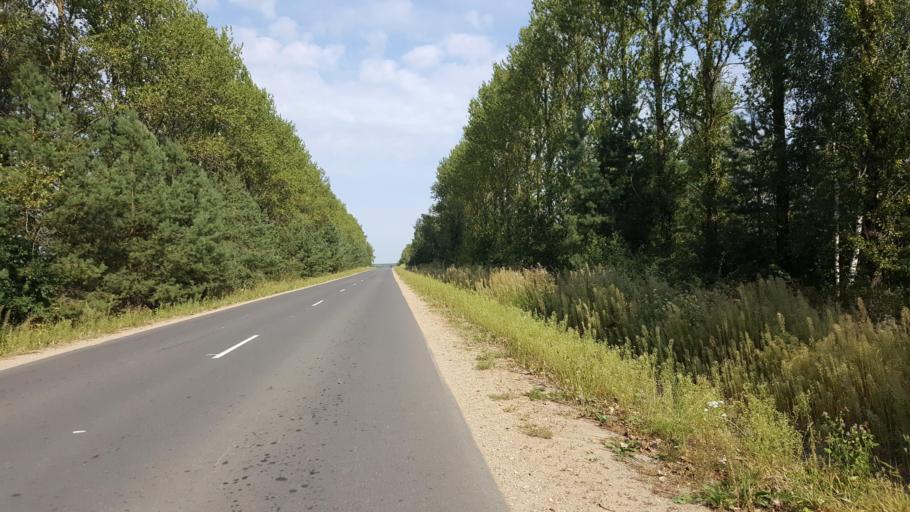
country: BY
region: Brest
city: Kamyanyets
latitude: 52.4535
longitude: 23.7362
